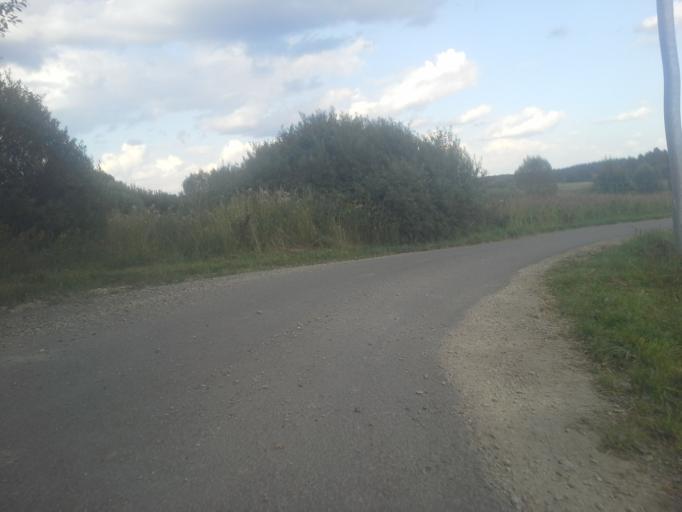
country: RU
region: Moskovskaya
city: Aprelevka
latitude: 55.4361
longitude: 37.0652
